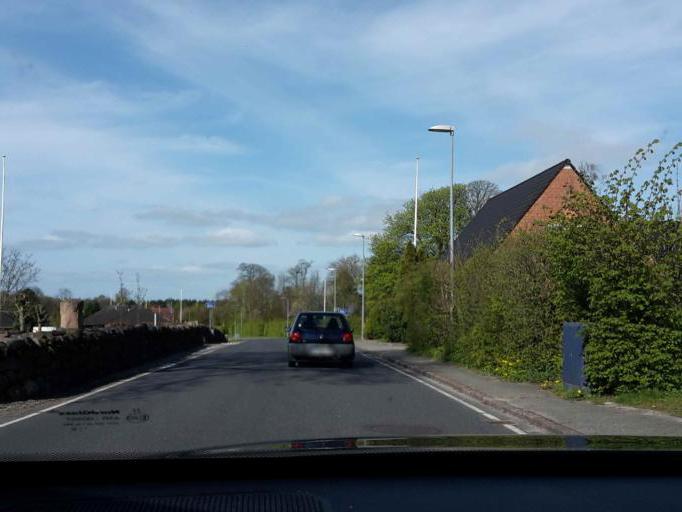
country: DK
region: South Denmark
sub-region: Vejen Kommune
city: Vejen
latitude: 55.5231
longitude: 9.1154
